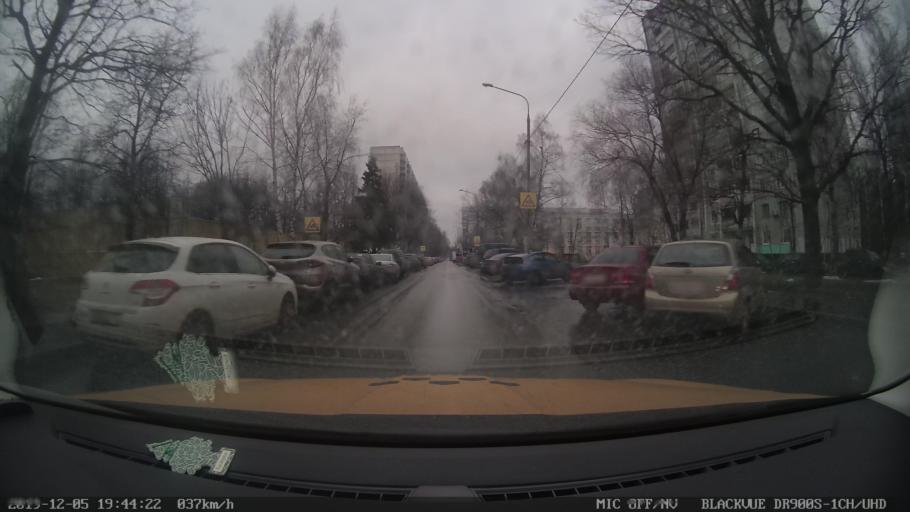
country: RU
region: Moscow
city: Lianozovo
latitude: 55.8994
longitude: 37.5769
